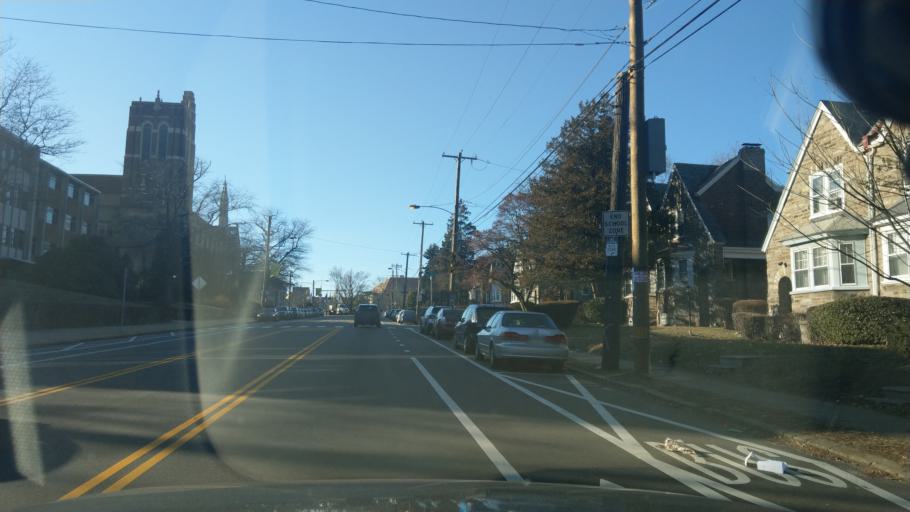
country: US
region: Pennsylvania
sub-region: Montgomery County
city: Wyncote
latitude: 40.0392
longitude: -75.1521
